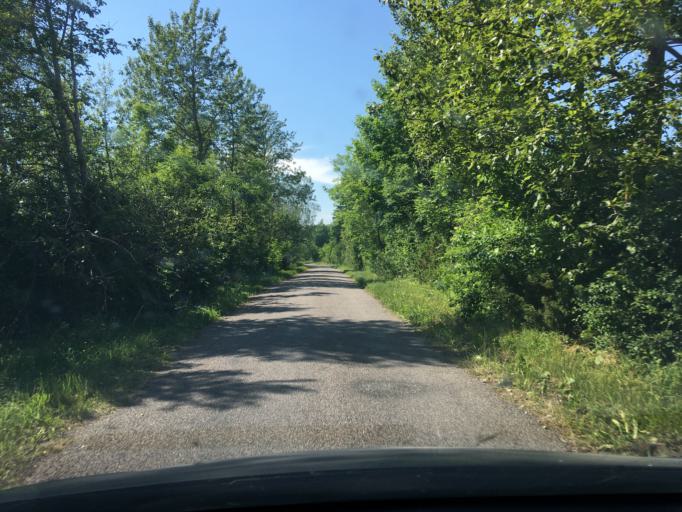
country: EE
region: Laeaene
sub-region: Lihula vald
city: Lihula
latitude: 58.5792
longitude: 23.6012
